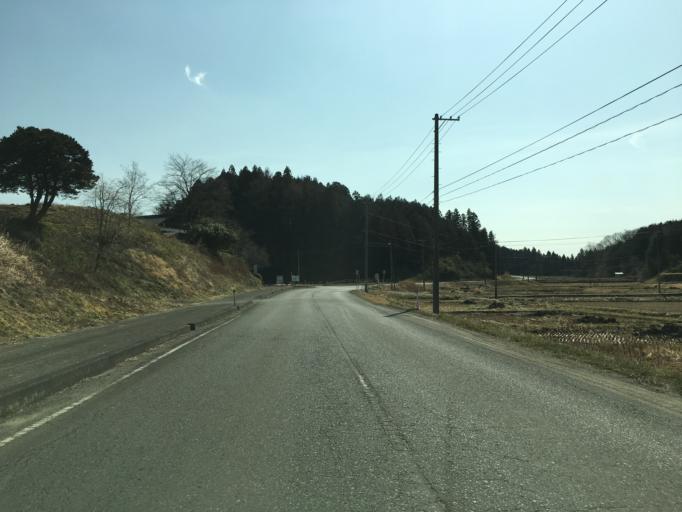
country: JP
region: Fukushima
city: Ishikawa
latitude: 37.1337
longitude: 140.4097
